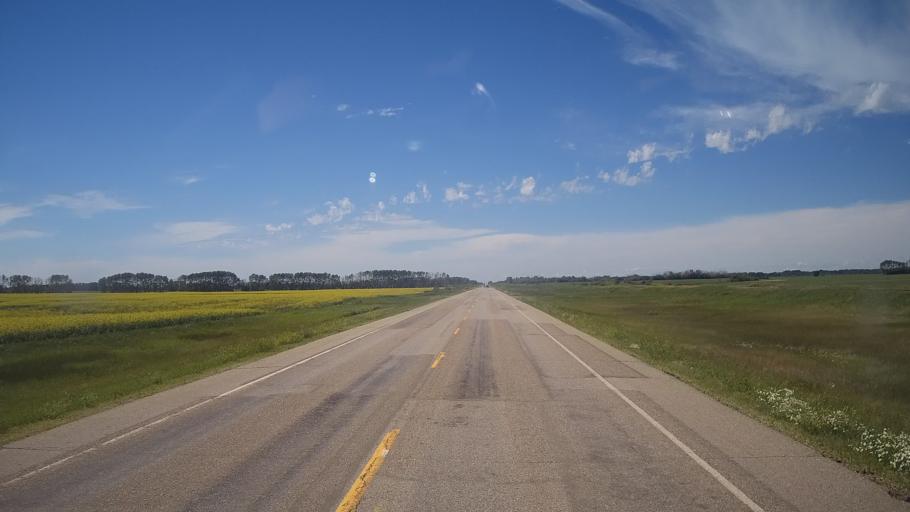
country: CA
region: Saskatchewan
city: Langenburg
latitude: 50.7873
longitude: -101.5384
